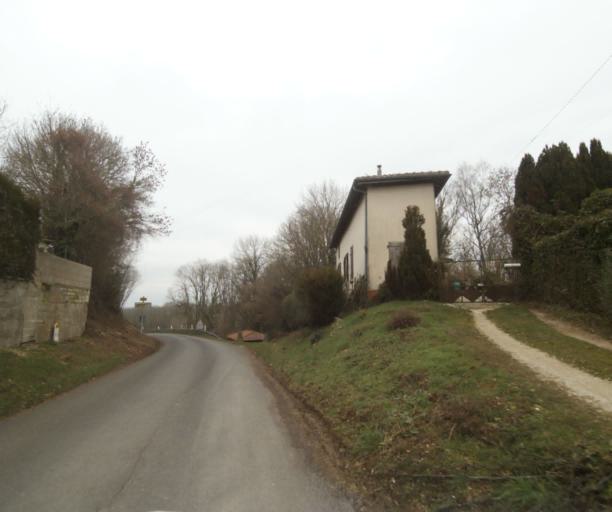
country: FR
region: Champagne-Ardenne
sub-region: Departement de la Haute-Marne
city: Villiers-en-Lieu
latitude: 48.6350
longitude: 4.8377
